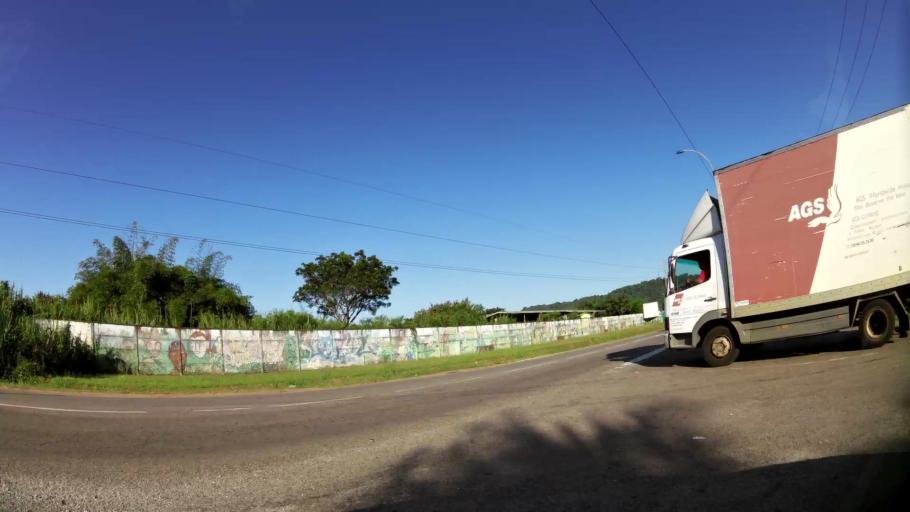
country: GF
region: Guyane
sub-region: Guyane
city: Remire-Montjoly
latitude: 4.8901
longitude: -52.2877
